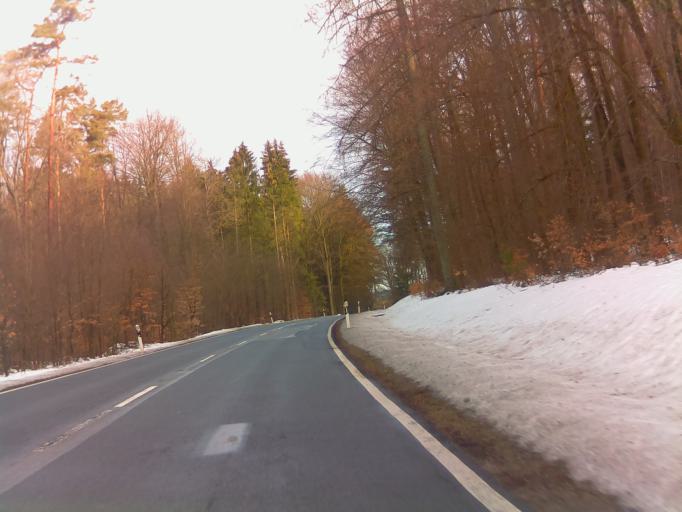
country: DE
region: Baden-Wuerttemberg
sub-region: Karlsruhe Region
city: Fahrenbach
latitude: 49.4897
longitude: 9.1457
